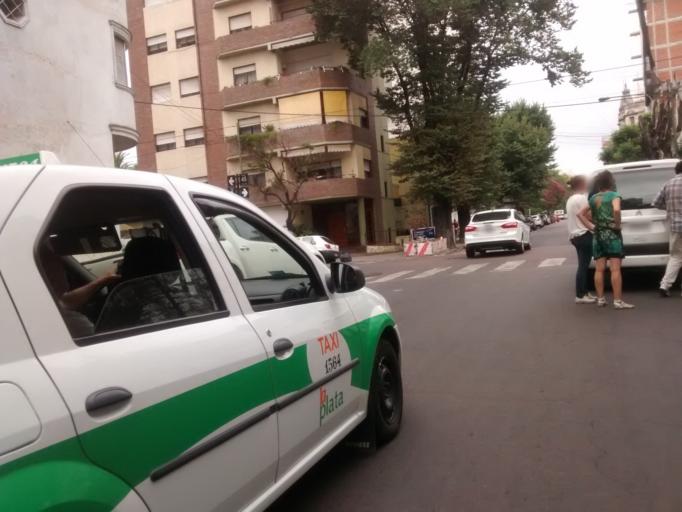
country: AR
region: Buenos Aires
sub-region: Partido de La Plata
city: La Plata
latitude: -34.9096
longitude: -57.9523
